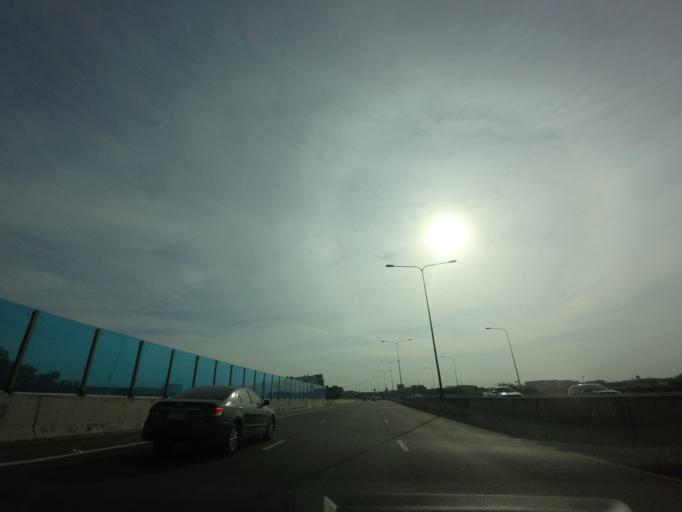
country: TH
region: Bangkok
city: Bang Khen
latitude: 13.8603
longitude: 100.6439
